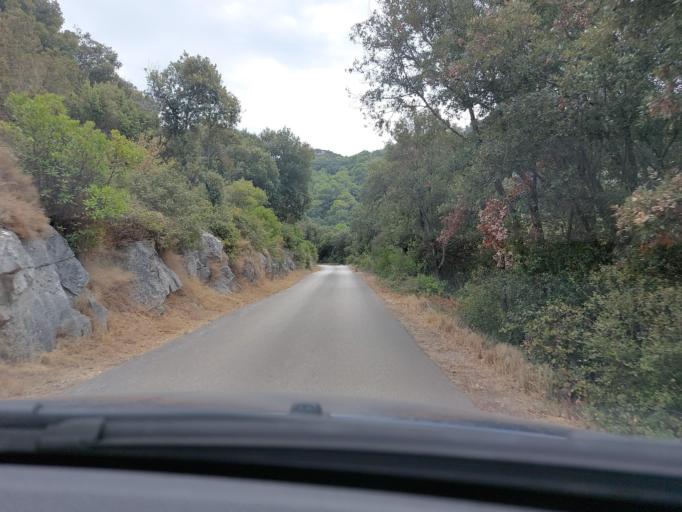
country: HR
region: Dubrovacko-Neretvanska
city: Smokvica
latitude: 42.7573
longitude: 16.9163
